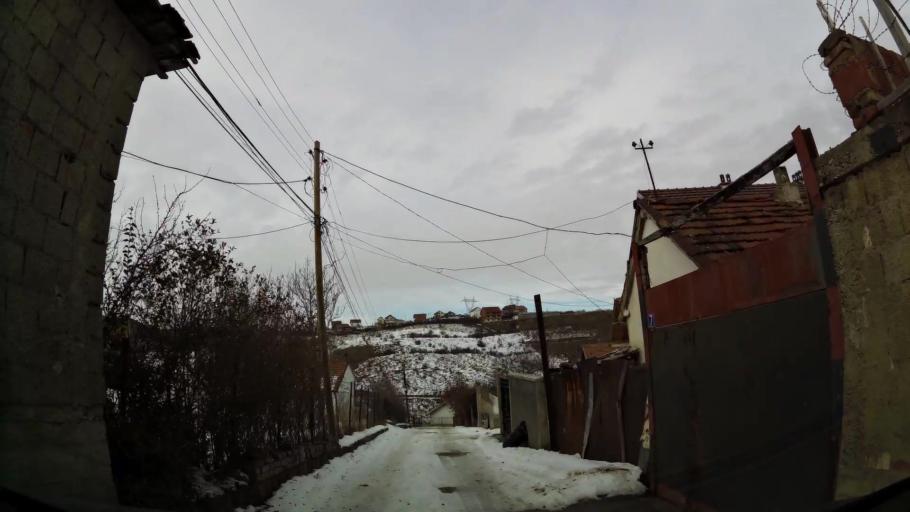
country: XK
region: Pristina
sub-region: Komuna e Prishtines
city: Pristina
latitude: 42.6899
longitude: 21.1732
